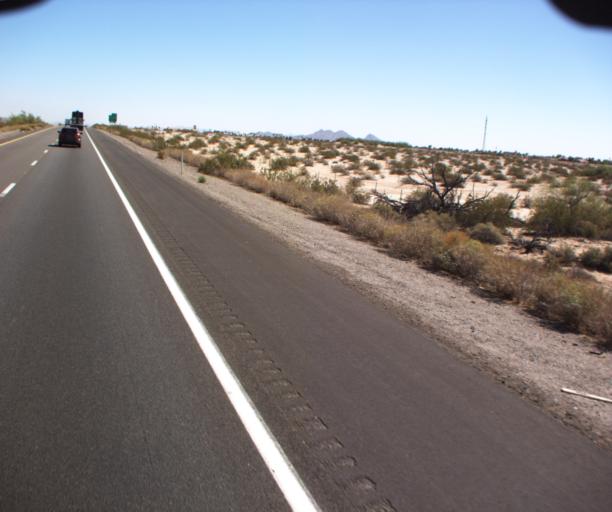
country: US
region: Arizona
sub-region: Yuma County
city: Wellton
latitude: 32.6582
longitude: -114.1570
